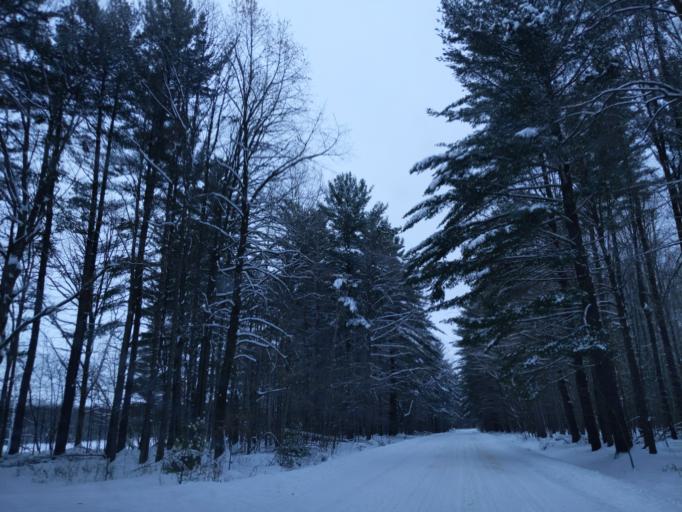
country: US
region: Wisconsin
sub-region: Marathon County
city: Marathon
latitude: 44.7673
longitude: -89.8694
